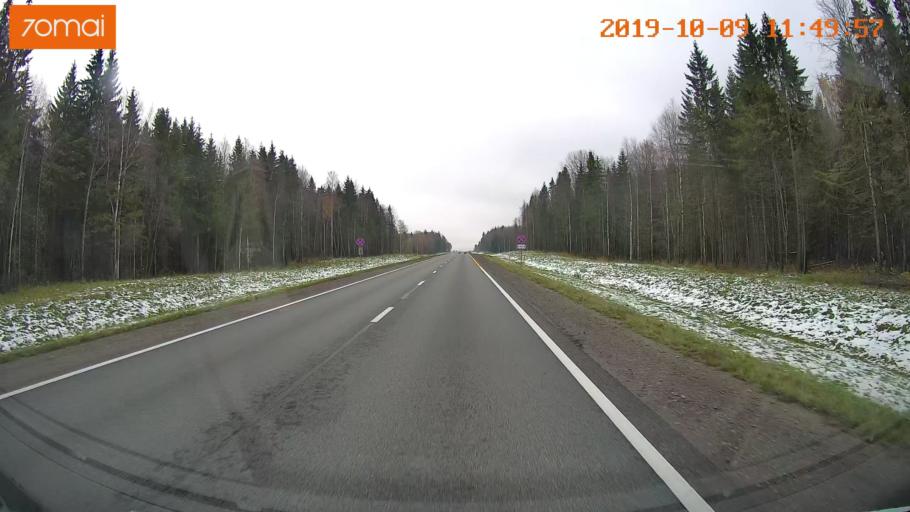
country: RU
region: Vologda
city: Gryazovets
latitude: 58.8118
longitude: 40.2386
